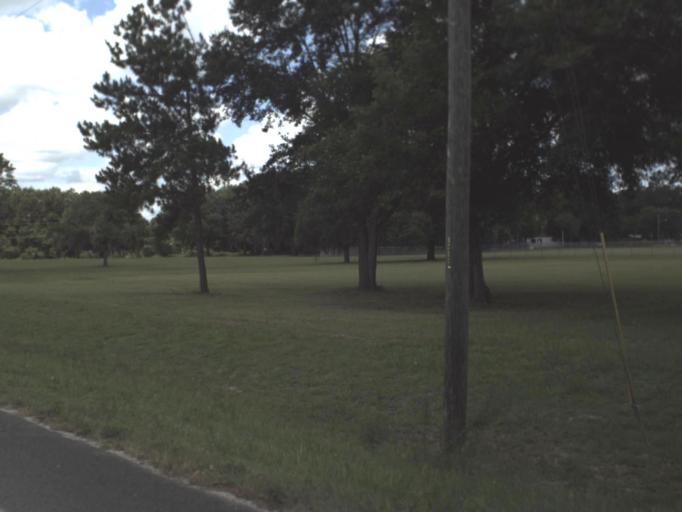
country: US
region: Florida
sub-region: Taylor County
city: Perry
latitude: 30.1105
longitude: -83.5934
